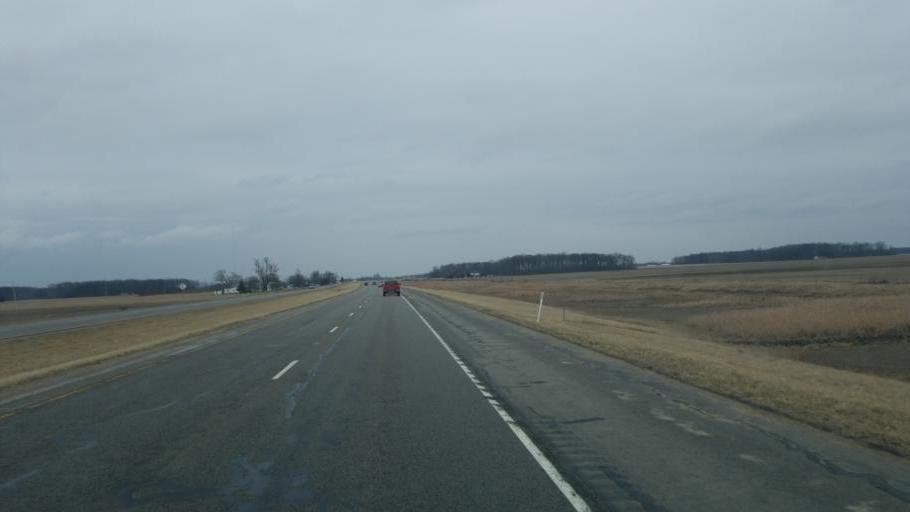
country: US
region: Indiana
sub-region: Adams County
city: Decatur
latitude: 40.7839
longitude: -84.9375
